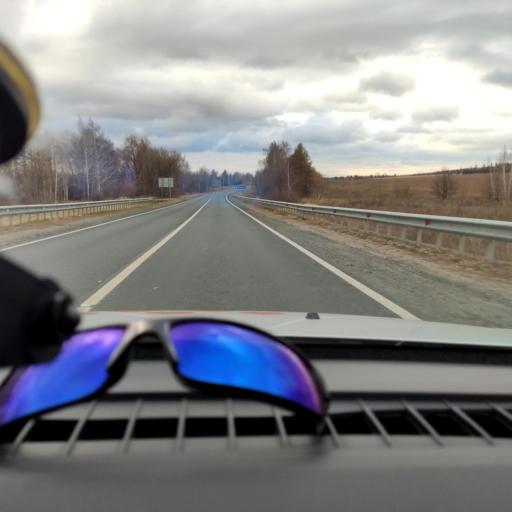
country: RU
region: Samara
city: Bereza
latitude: 53.4849
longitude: 50.1168
